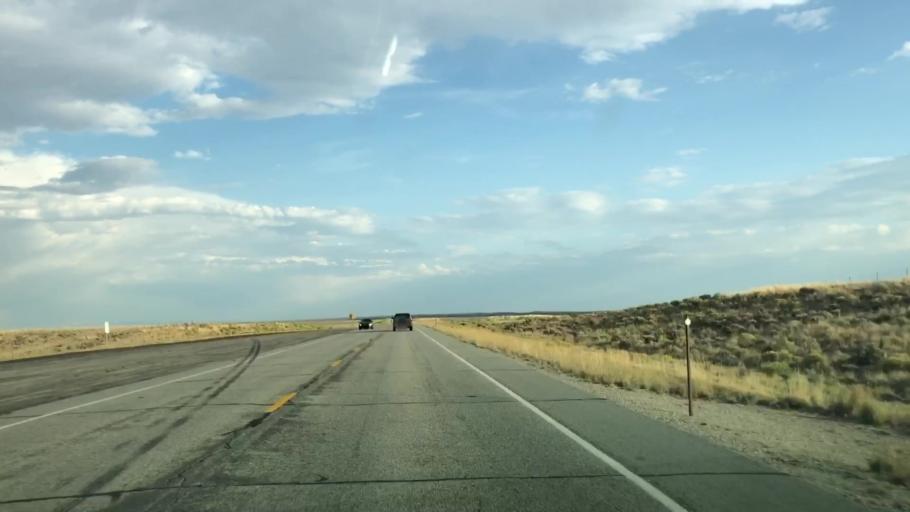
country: US
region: Wyoming
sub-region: Sublette County
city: Marbleton
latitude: 42.3278
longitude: -109.5139
